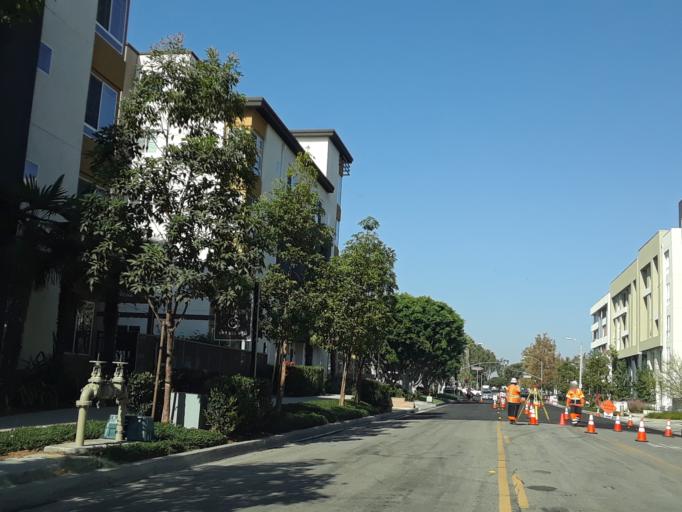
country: US
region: California
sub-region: Orange County
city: Irvine
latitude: 33.6824
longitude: -117.8355
